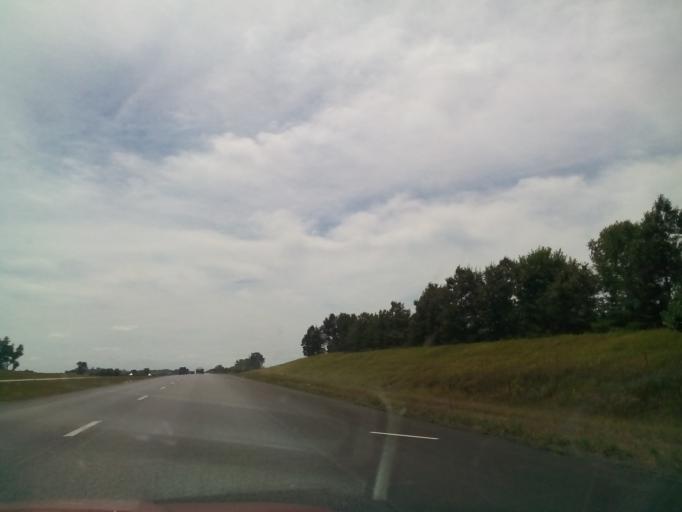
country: US
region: Illinois
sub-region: Ogle County
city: Davis Junction
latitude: 42.1459
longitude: -89.0236
